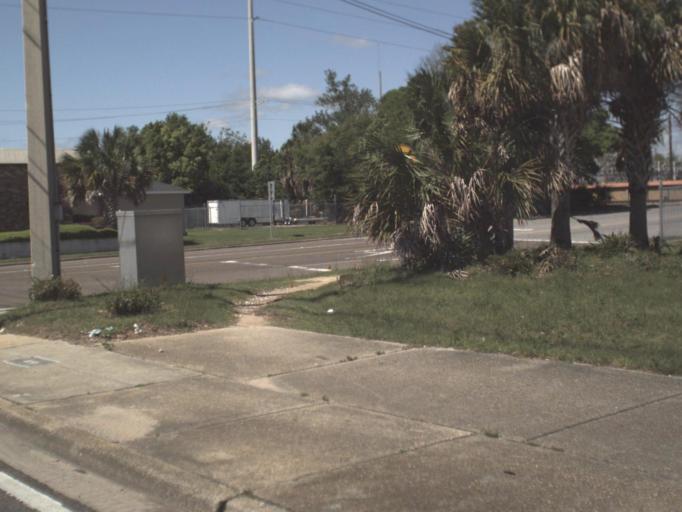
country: US
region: Florida
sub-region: Escambia County
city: Goulding
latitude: 30.4385
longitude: -87.2214
